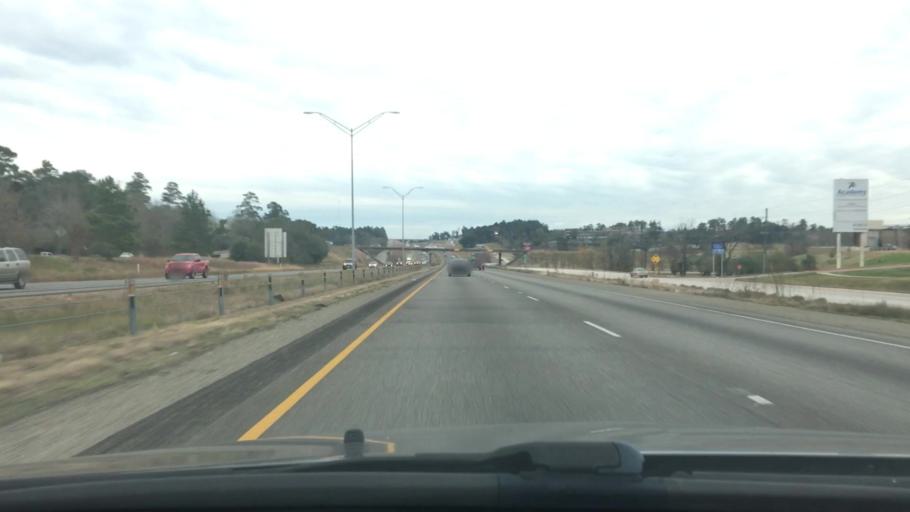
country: US
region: Texas
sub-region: Walker County
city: Huntsville
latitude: 30.7080
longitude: -95.5631
